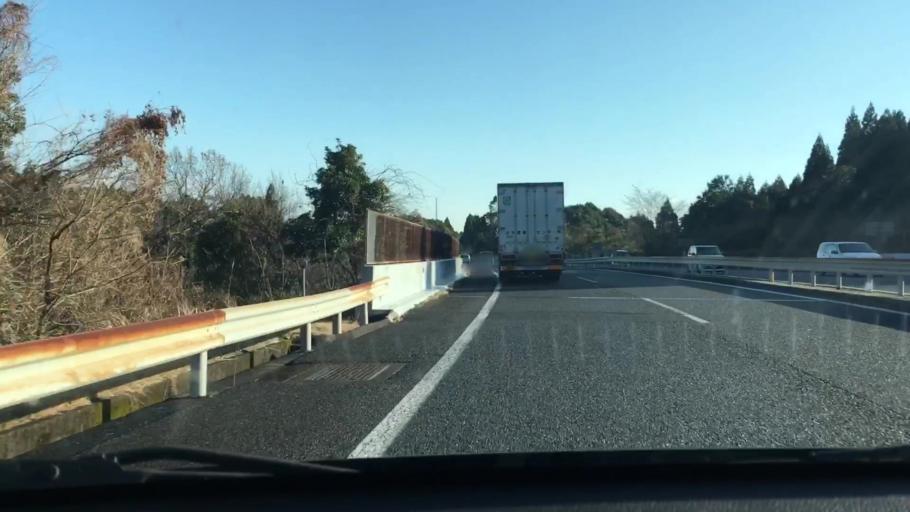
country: JP
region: Kagoshima
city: Kajiki
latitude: 31.8234
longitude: 130.6941
